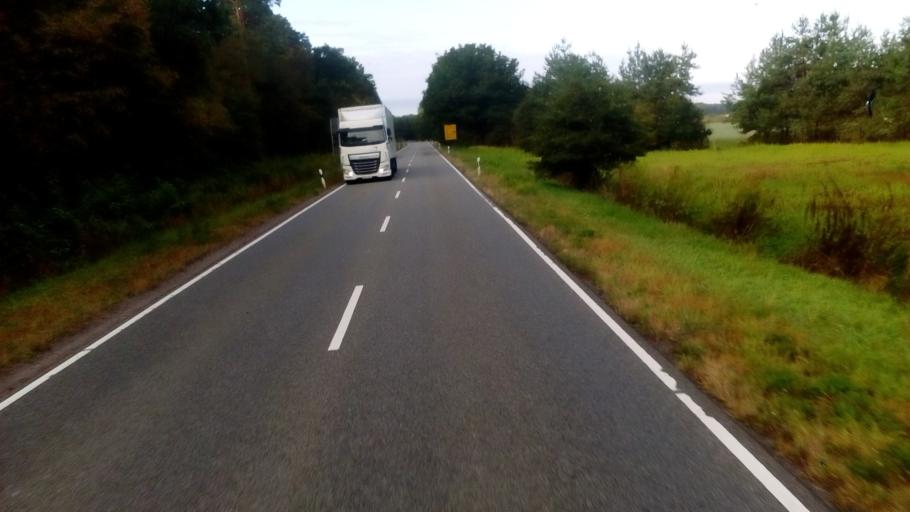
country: DE
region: Rheinland-Pfalz
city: Berg
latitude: 49.0232
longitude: 8.1974
